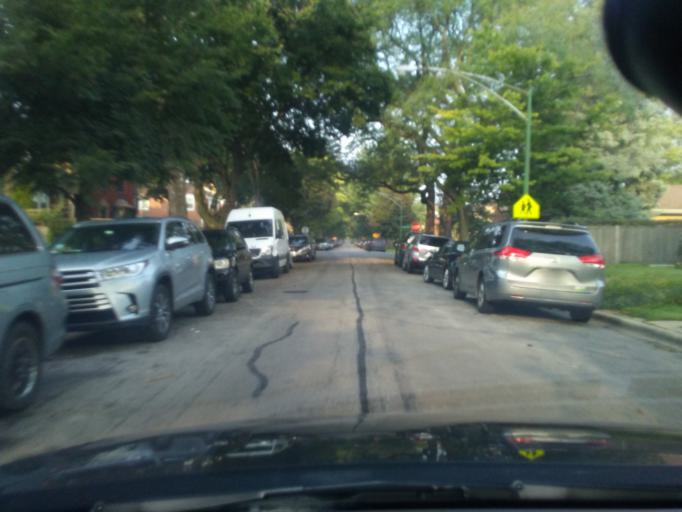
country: US
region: Illinois
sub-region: Cook County
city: Evanston
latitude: 42.0148
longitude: -87.7013
